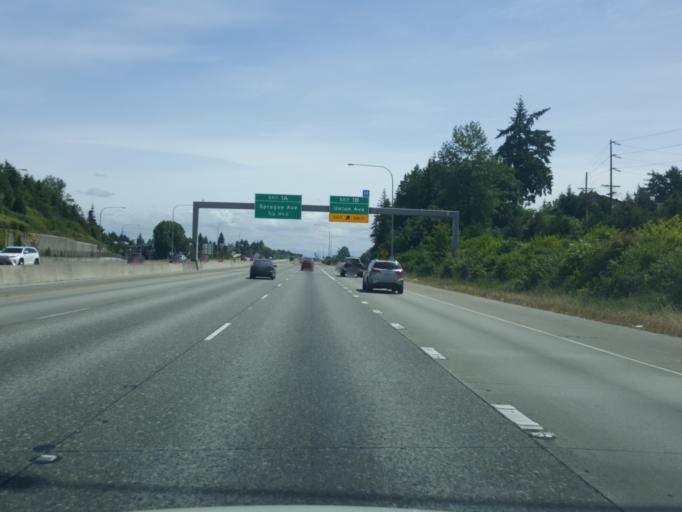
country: US
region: Washington
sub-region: Pierce County
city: Fircrest
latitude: 47.2346
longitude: -122.4873
